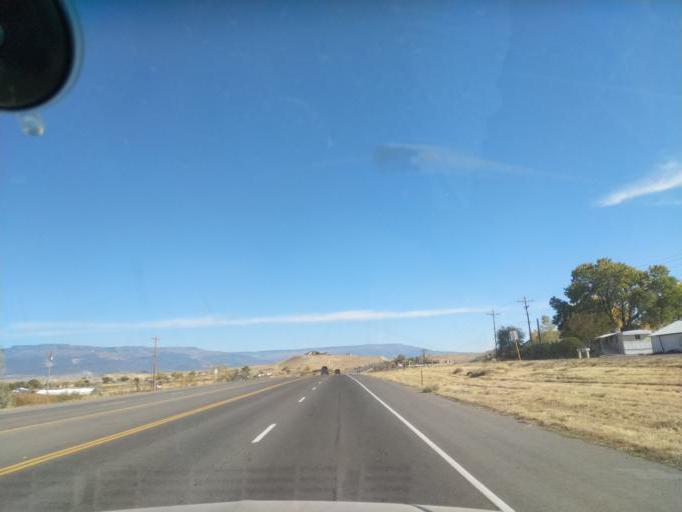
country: US
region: Colorado
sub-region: Mesa County
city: Fruitvale
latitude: 39.0222
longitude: -108.4931
